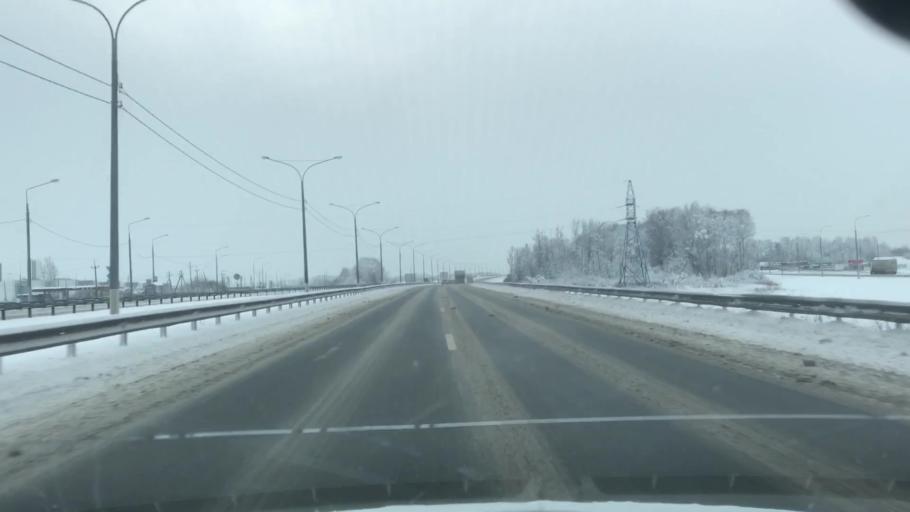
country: RU
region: Moskovskaya
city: Mikhnevo
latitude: 55.1553
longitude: 37.9287
